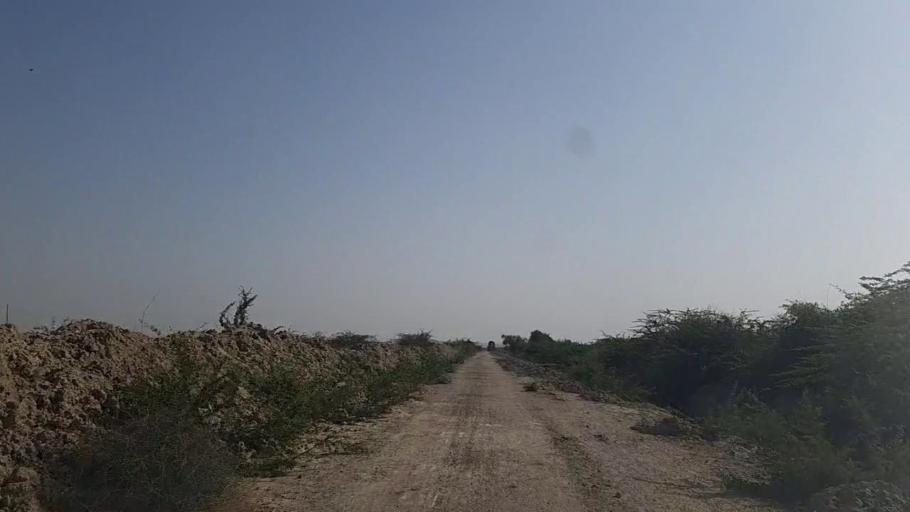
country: PK
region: Sindh
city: Kadhan
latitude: 24.5803
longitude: 69.2628
